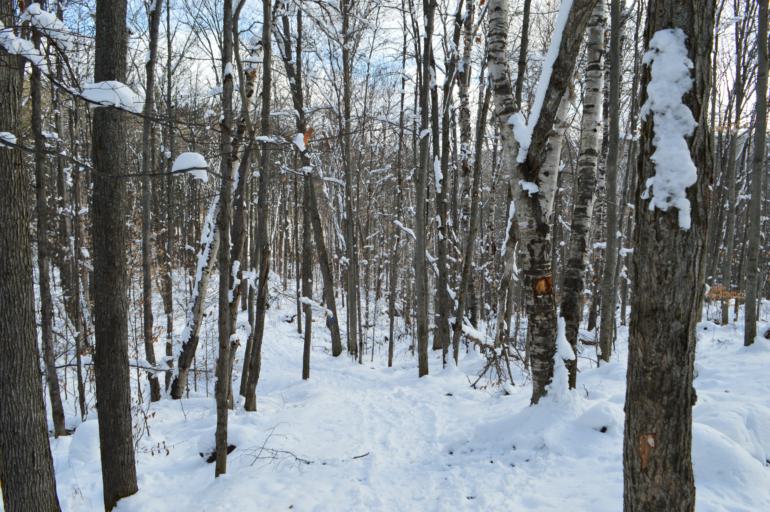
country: CA
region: Ontario
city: Bancroft
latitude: 45.5821
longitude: -78.4097
